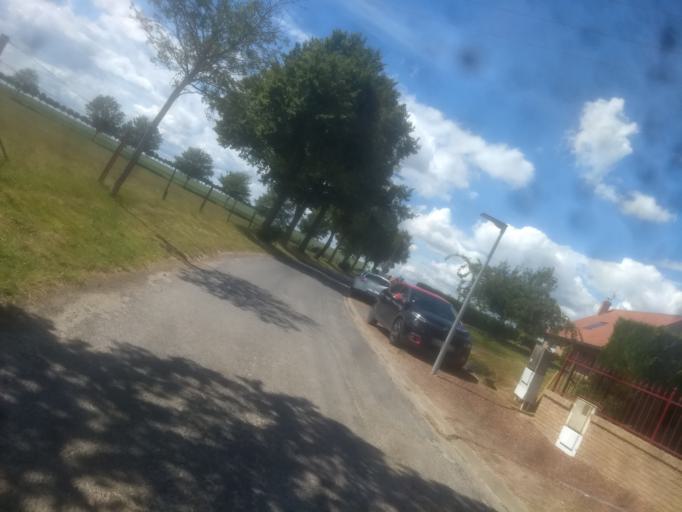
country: FR
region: Nord-Pas-de-Calais
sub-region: Departement du Pas-de-Calais
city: Tilloy-les-Mofflaines
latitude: 50.2315
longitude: 2.8381
